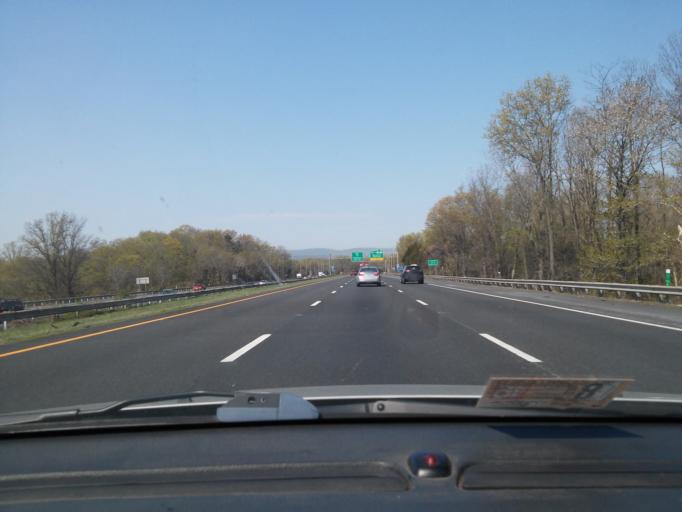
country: US
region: New Jersey
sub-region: Somerset County
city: Bedminster
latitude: 40.6439
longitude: -74.6312
